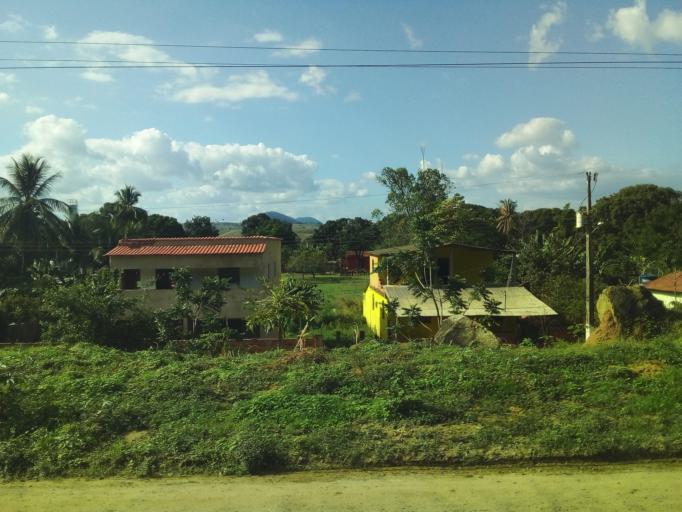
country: BR
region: Minas Gerais
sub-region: Conselheiro Pena
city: Conselheiro Pena
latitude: -19.0126
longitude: -41.5464
